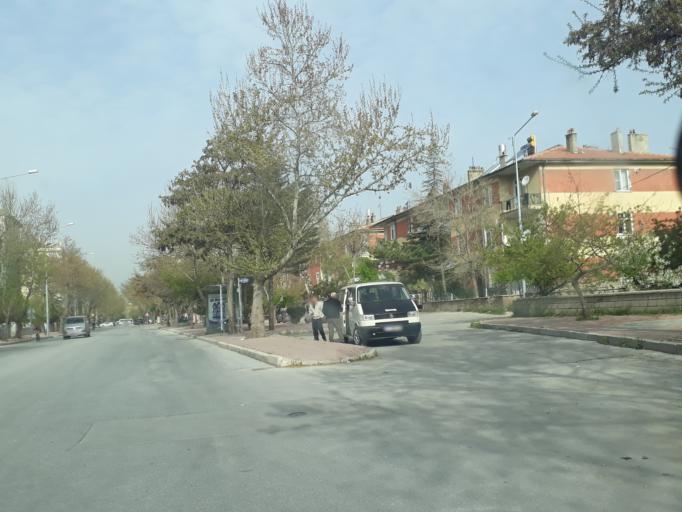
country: TR
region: Konya
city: Selcuklu
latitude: 37.9326
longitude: 32.4975
